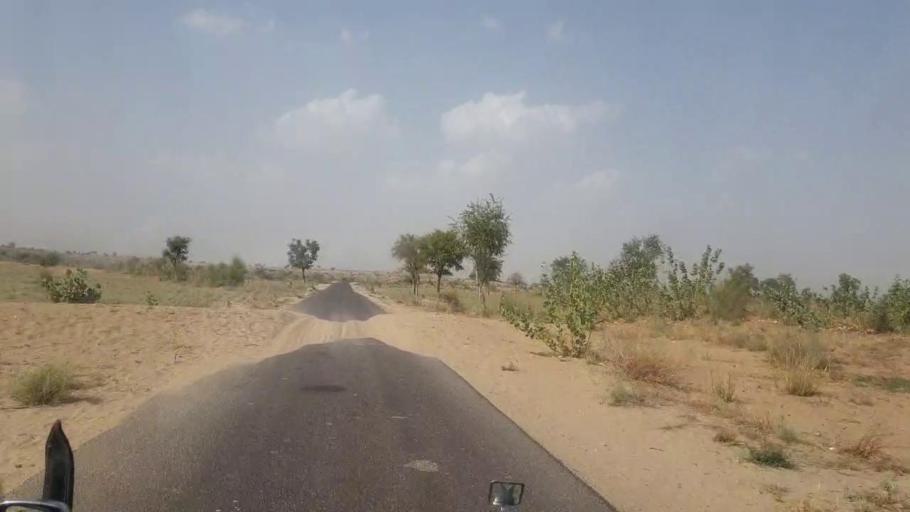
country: PK
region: Sindh
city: Islamkot
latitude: 25.2015
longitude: 70.2837
